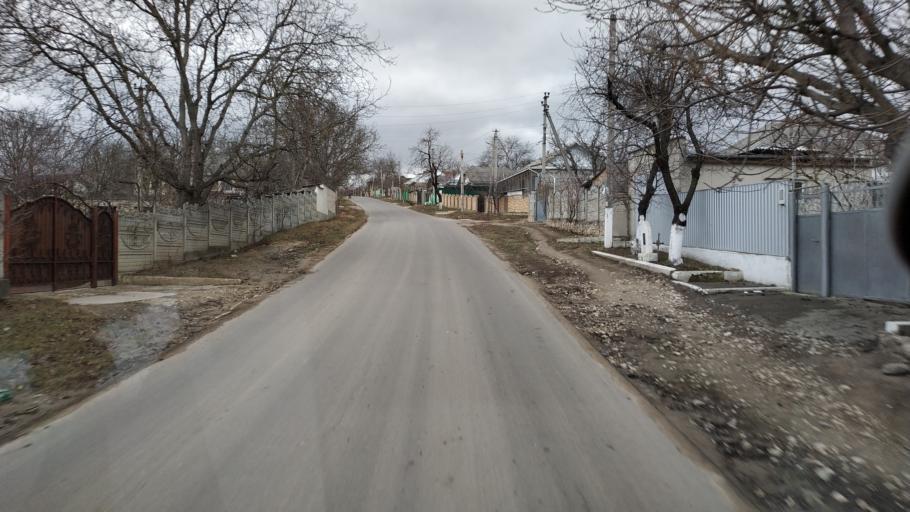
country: MD
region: Calarasi
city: Calarasi
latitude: 47.2444
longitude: 28.2847
